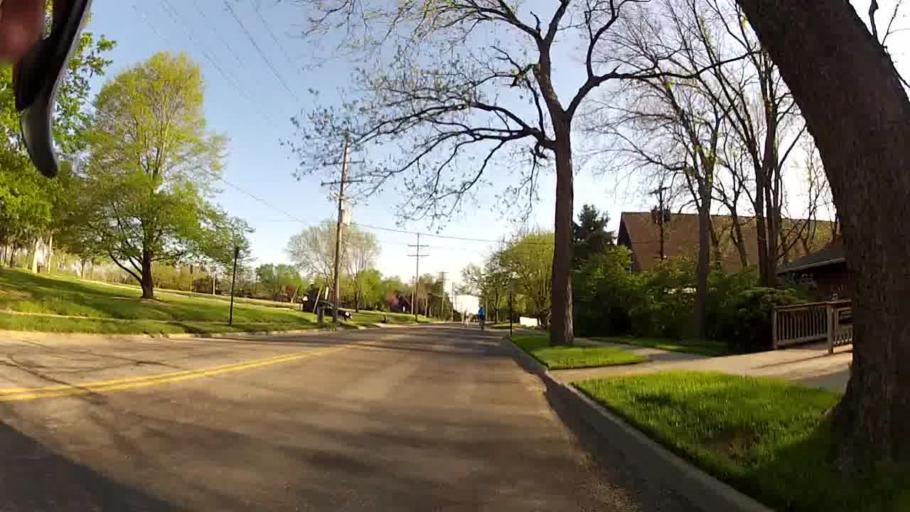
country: US
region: Kansas
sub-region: Riley County
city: Manhattan
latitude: 39.1826
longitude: -96.5887
